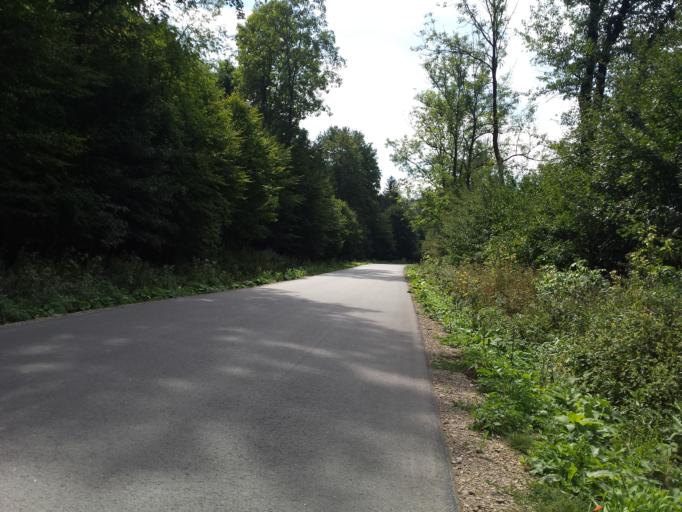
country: PL
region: Subcarpathian Voivodeship
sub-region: Powiat przemyski
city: Fredropol
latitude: 49.6282
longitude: 22.6421
